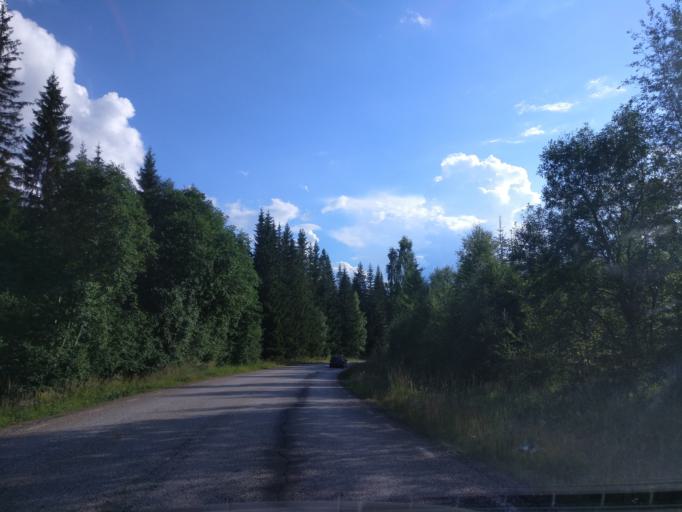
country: SE
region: Dalarna
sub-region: Ludvika Kommun
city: Ludvika
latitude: 60.2725
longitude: 15.0720
